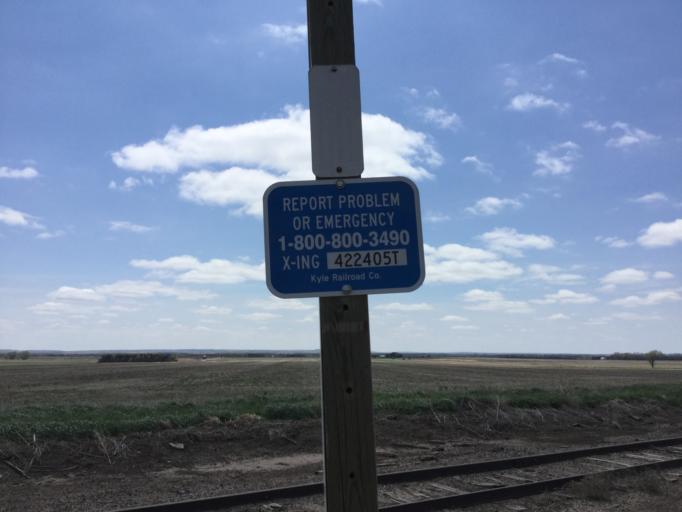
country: US
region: Kansas
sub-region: Osborne County
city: Osborne
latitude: 39.4516
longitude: -98.6035
